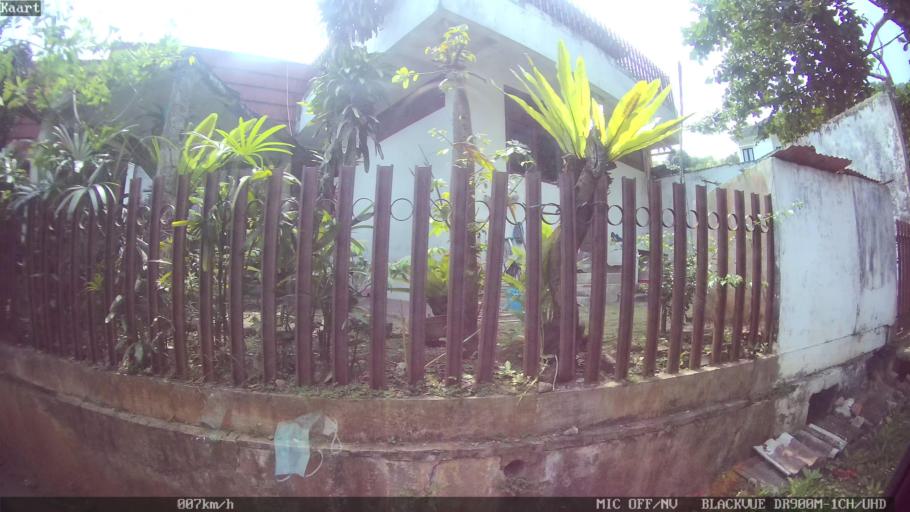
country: ID
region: Lampung
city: Bandarlampung
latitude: -5.4332
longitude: 105.2686
